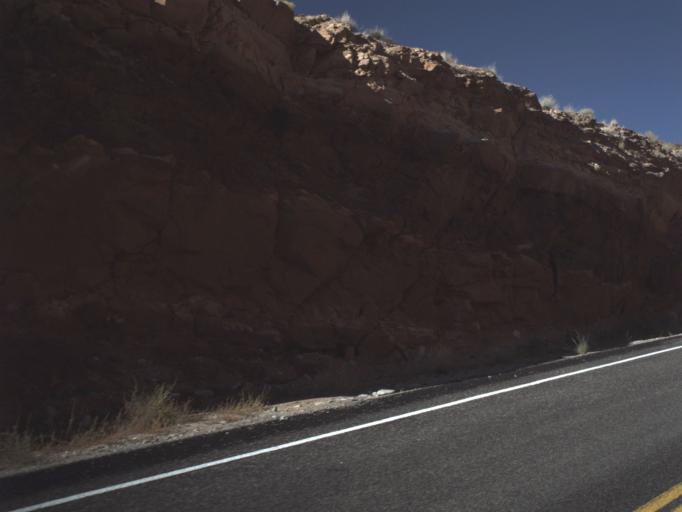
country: US
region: Utah
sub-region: San Juan County
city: Blanding
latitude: 37.8895
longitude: -110.4103
